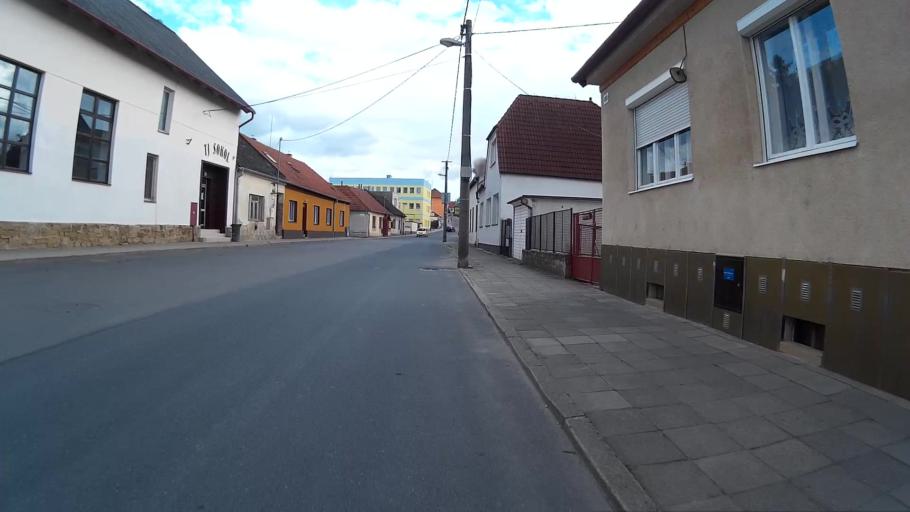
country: CZ
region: South Moravian
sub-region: Okres Brno-Venkov
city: Rosice
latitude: 49.1846
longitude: 16.3924
